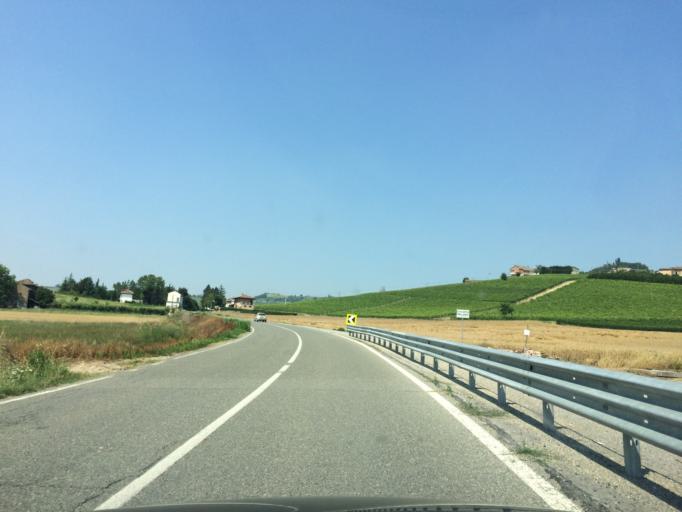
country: IT
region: Piedmont
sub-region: Provincia di Asti
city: Agliano Terme
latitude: 44.7763
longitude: 8.2290
